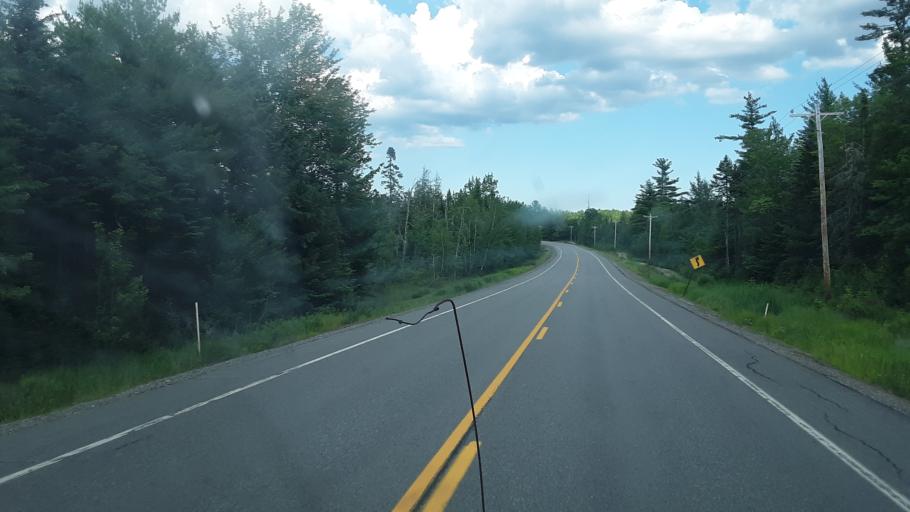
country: US
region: Maine
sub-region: Washington County
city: Machias
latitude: 45.0001
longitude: -67.6094
